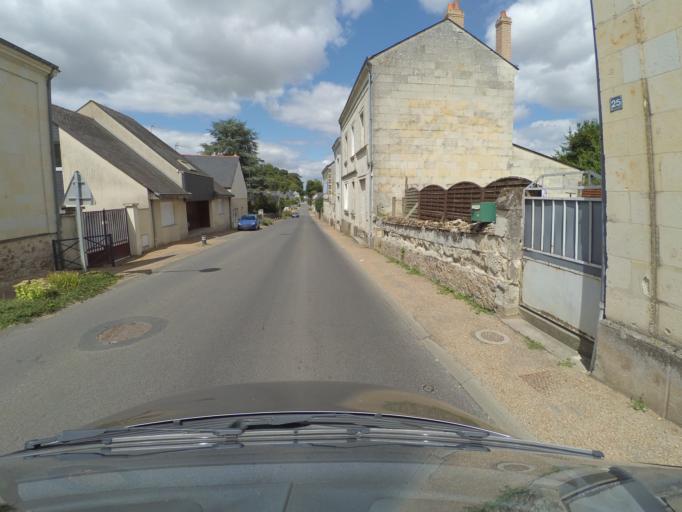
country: FR
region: Pays de la Loire
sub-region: Departement de Maine-et-Loire
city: Gennes
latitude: 47.3385
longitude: -0.2311
